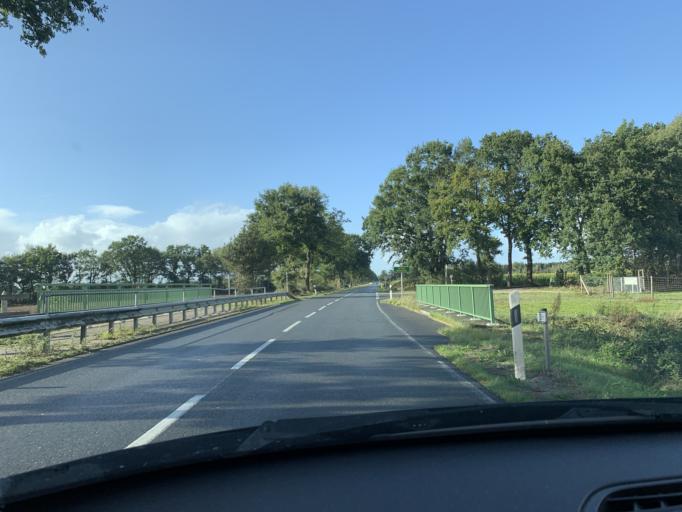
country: DE
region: Lower Saxony
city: Bad Zwischenahn
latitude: 53.1835
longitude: 7.9290
